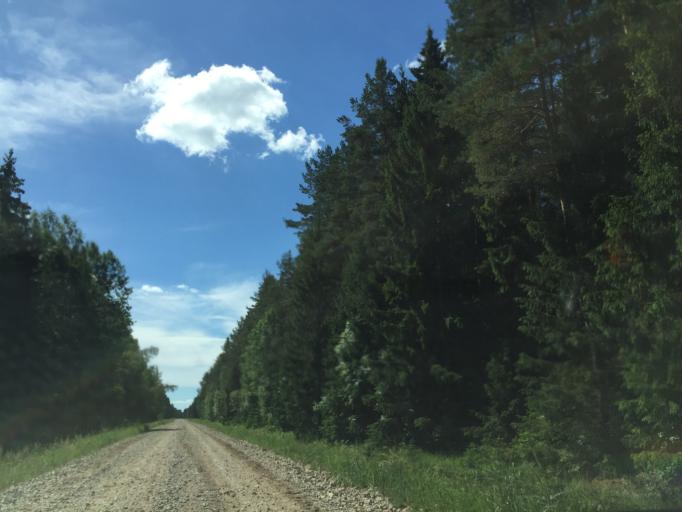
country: LV
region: Ventspils Rajons
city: Piltene
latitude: 57.2651
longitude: 21.8359
